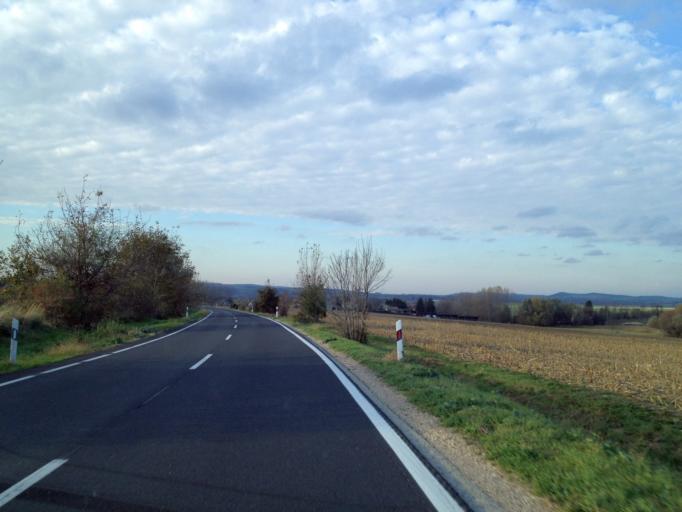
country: HU
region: Gyor-Moson-Sopron
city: Bakonyszentlaszlo
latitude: 47.4265
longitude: 17.8388
